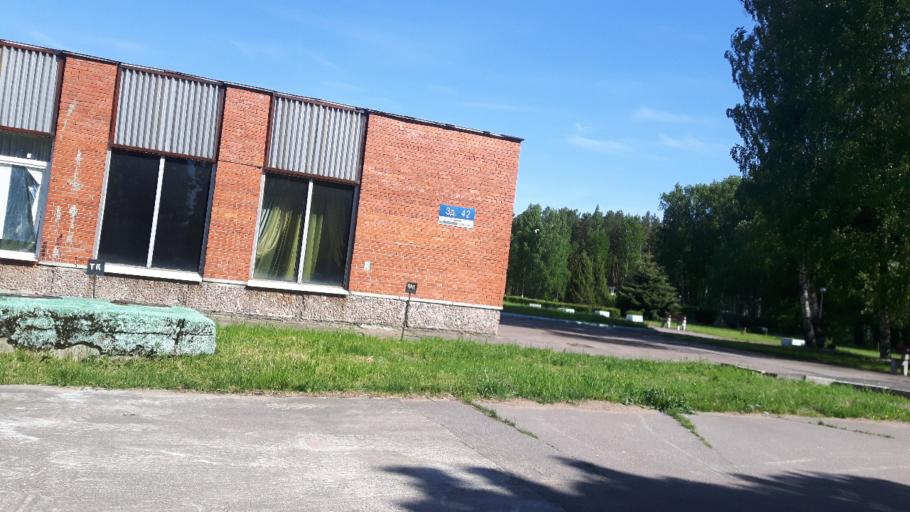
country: RU
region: Leningrad
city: Sista-Palkino
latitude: 59.7630
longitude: 28.7402
